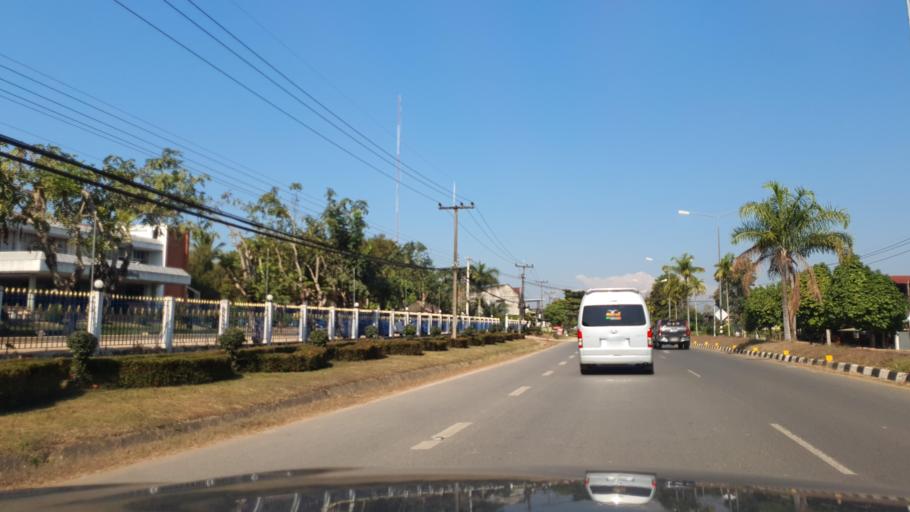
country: TH
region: Nan
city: Pua
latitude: 19.1659
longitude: 100.9248
